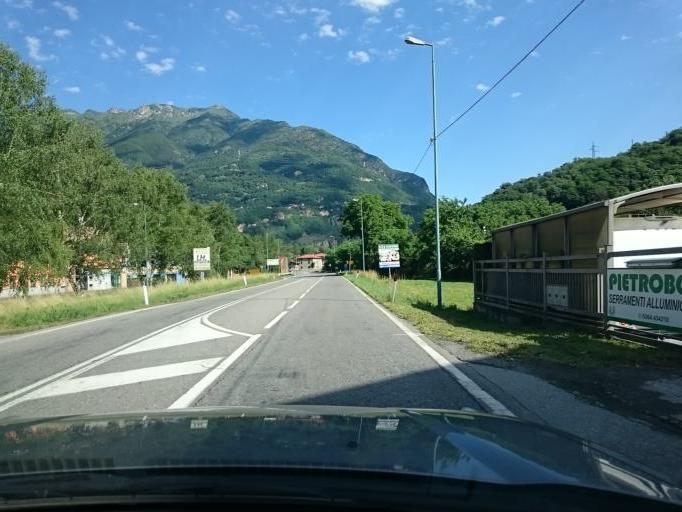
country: IT
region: Lombardy
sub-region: Provincia di Brescia
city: Capo di Ponte
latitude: 46.0192
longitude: 10.3468
